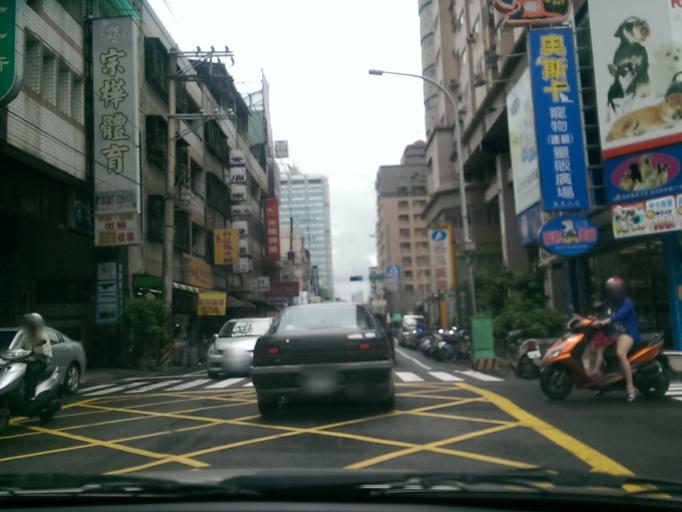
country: TW
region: Taiwan
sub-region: Taichung City
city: Taichung
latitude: 24.1730
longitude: 120.6450
